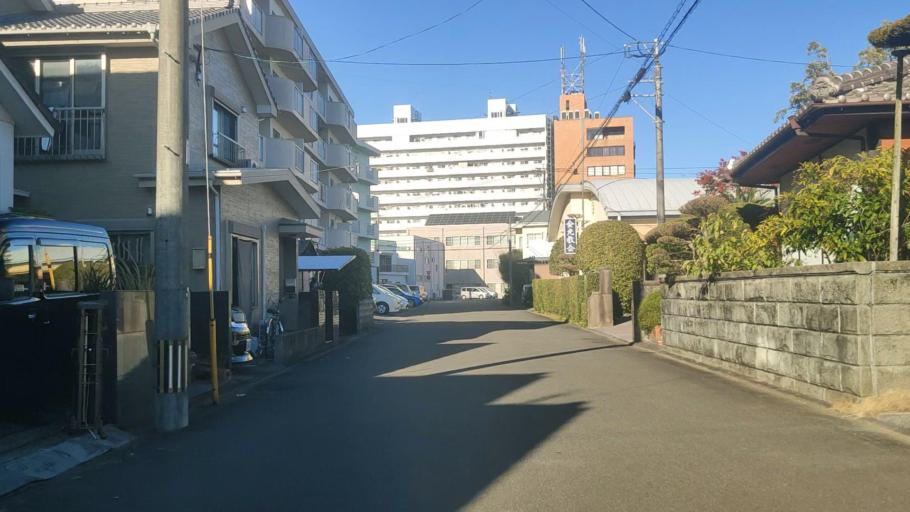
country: JP
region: Miyazaki
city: Miyazaki-shi
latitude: 31.9011
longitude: 131.4221
